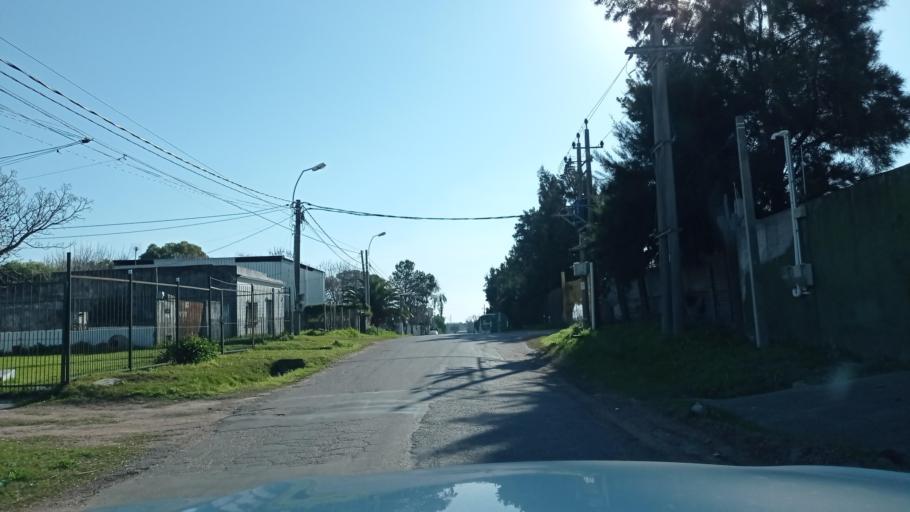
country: UY
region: Canelones
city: La Paz
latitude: -34.8354
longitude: -56.2470
